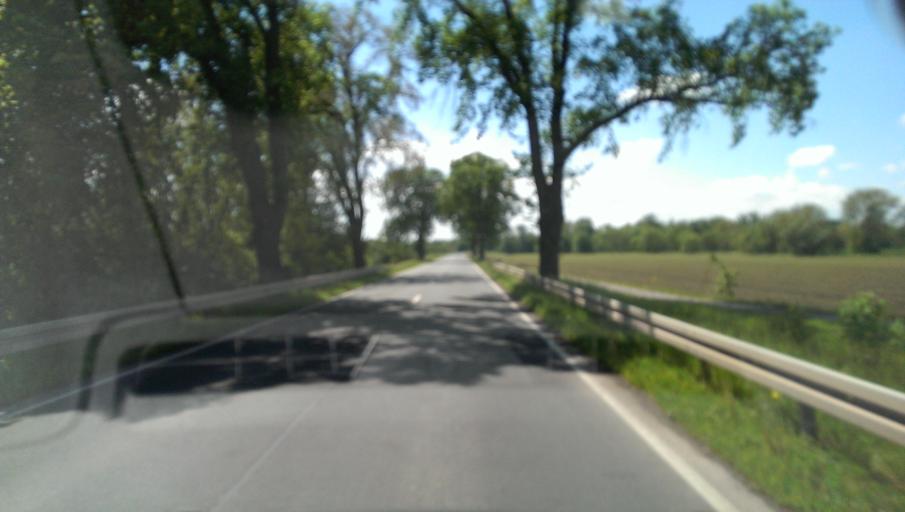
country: DE
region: Saxony-Anhalt
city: Hadmersleben
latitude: 52.0021
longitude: 11.3169
